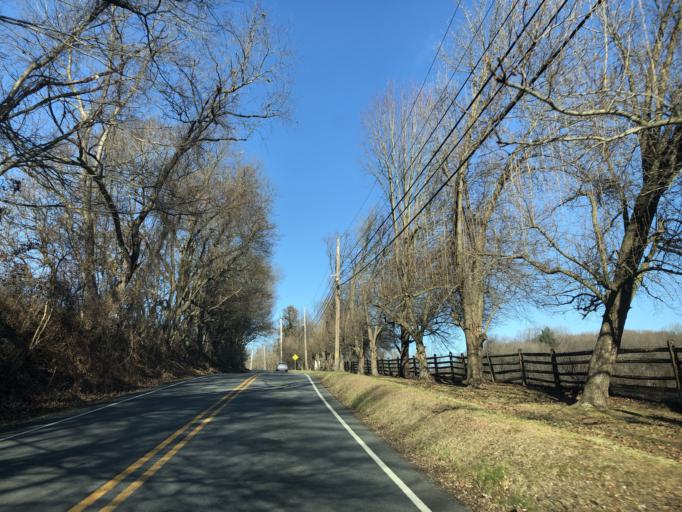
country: US
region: Pennsylvania
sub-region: Chester County
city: South Coatesville
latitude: 39.9352
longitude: -75.8308
